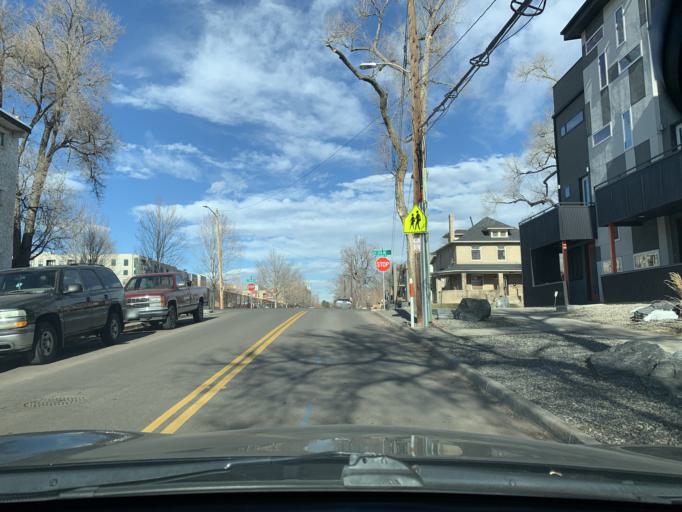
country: US
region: Colorado
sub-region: Denver County
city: Denver
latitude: 39.7545
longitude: -105.0205
